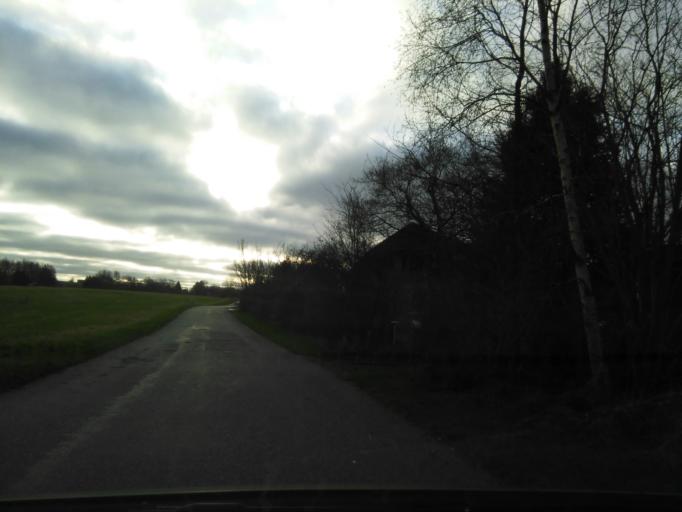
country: DK
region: Central Jutland
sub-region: Arhus Kommune
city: Framlev
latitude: 56.1756
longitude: 10.0451
